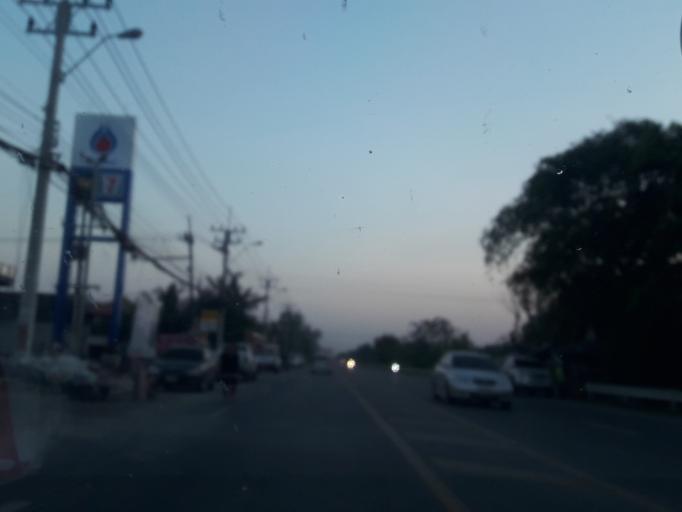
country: TH
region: Pathum Thani
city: Khlong Luang
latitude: 14.0844
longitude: 100.7103
